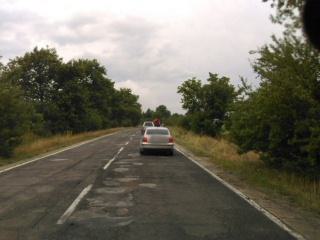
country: BG
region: Plovdiv
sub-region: Obshtina Karlovo
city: Karlovo
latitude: 42.5726
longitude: 24.8254
